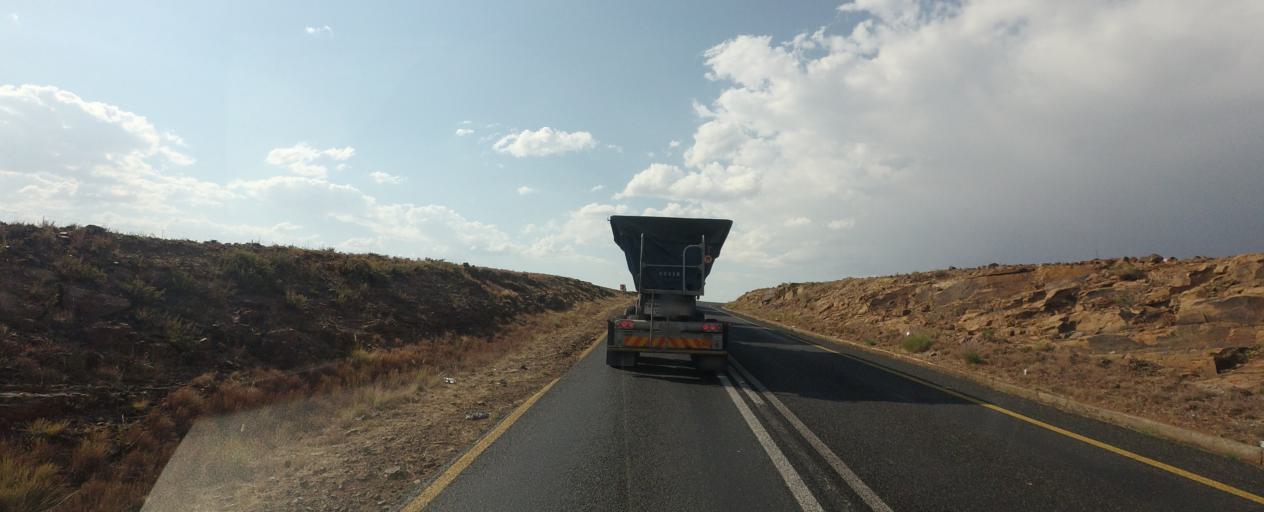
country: ZA
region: Mpumalanga
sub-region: Ehlanzeni District
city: Lydenburg
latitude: -25.1109
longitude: 30.5078
